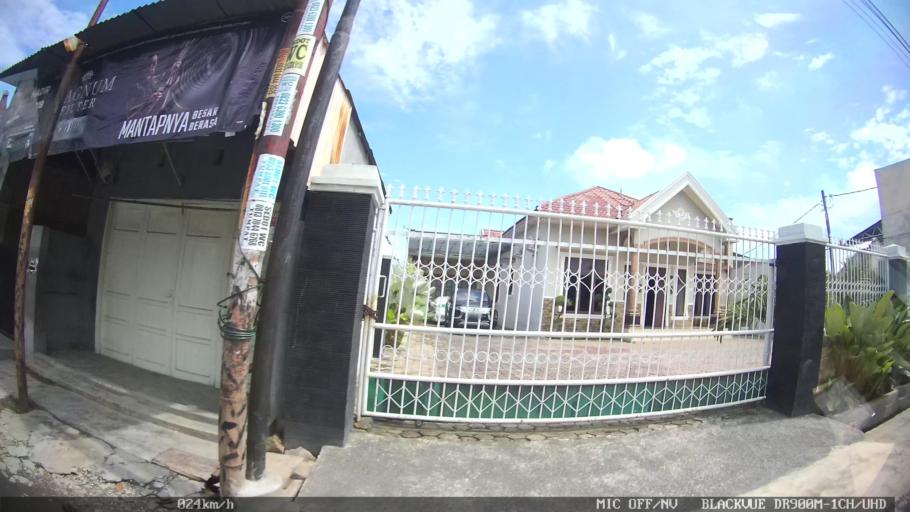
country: ID
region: North Sumatra
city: Medan
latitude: 3.5911
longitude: 98.7453
